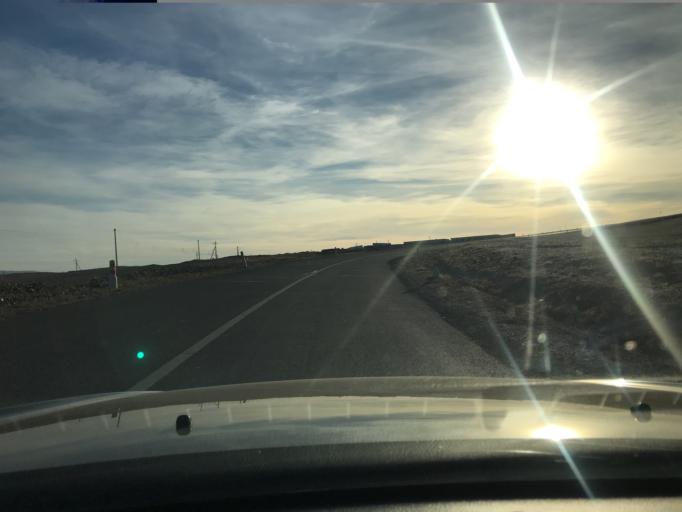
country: MN
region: Central Aimak
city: Dzuunmod
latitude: 47.7901
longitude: 107.3219
